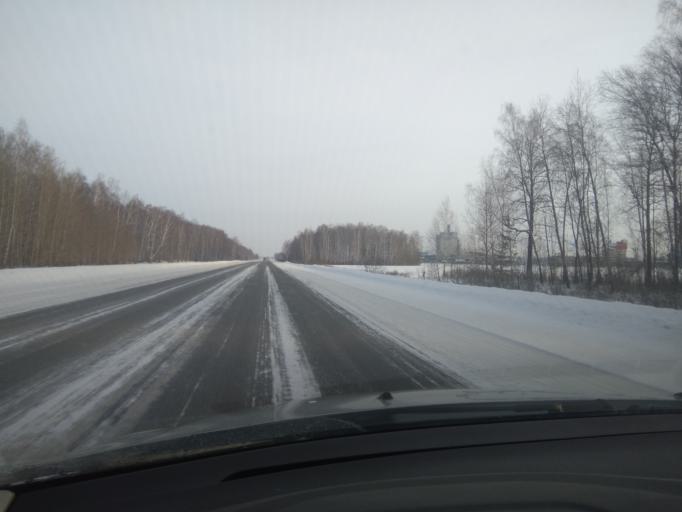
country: RU
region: Sverdlovsk
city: Bogdanovich
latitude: 56.8036
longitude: 62.0246
